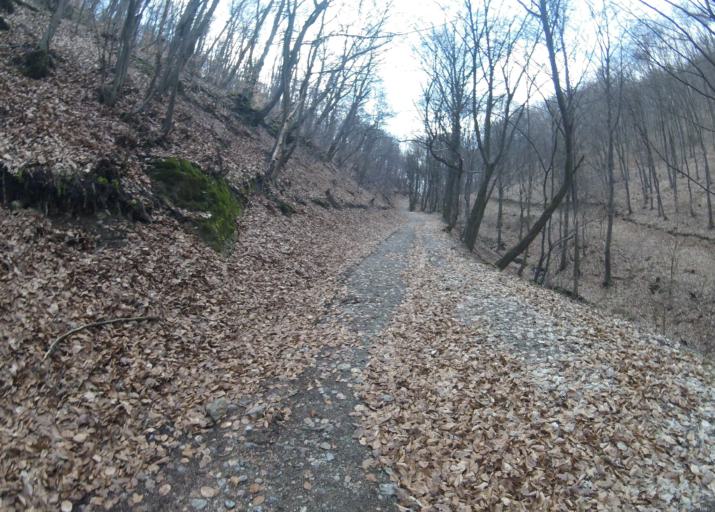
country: HU
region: Heves
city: Belapatfalva
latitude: 48.0361
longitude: 20.3534
